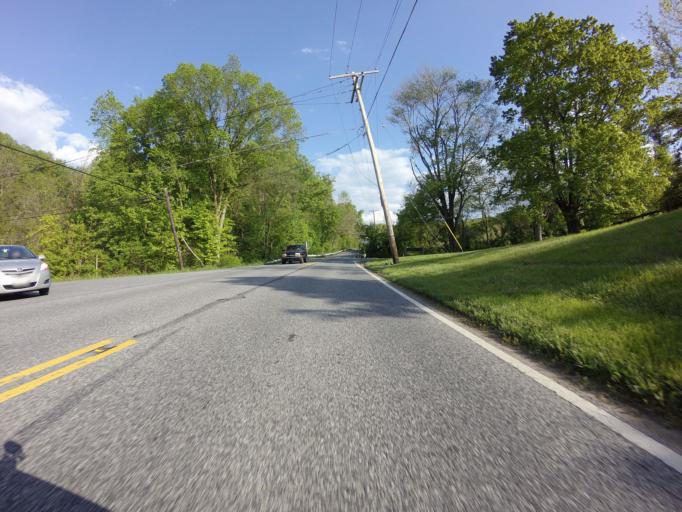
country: US
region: Maryland
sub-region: Baltimore County
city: Hunt Valley
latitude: 39.5183
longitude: -76.7188
